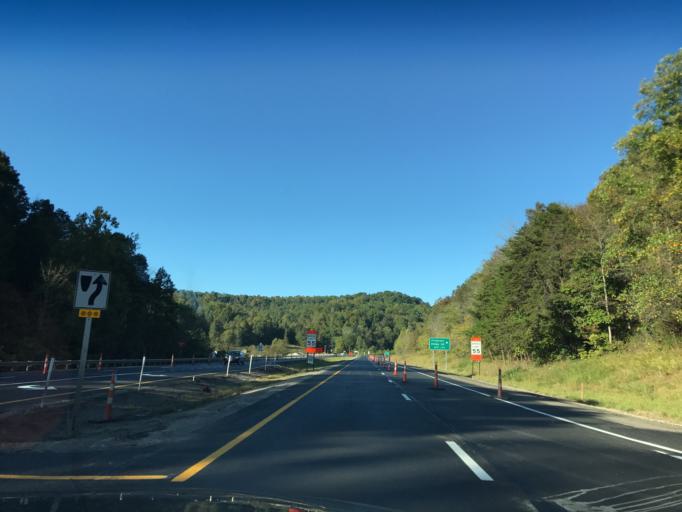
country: US
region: Ohio
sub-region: Washington County
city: Reno
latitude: 39.2466
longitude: -81.3611
